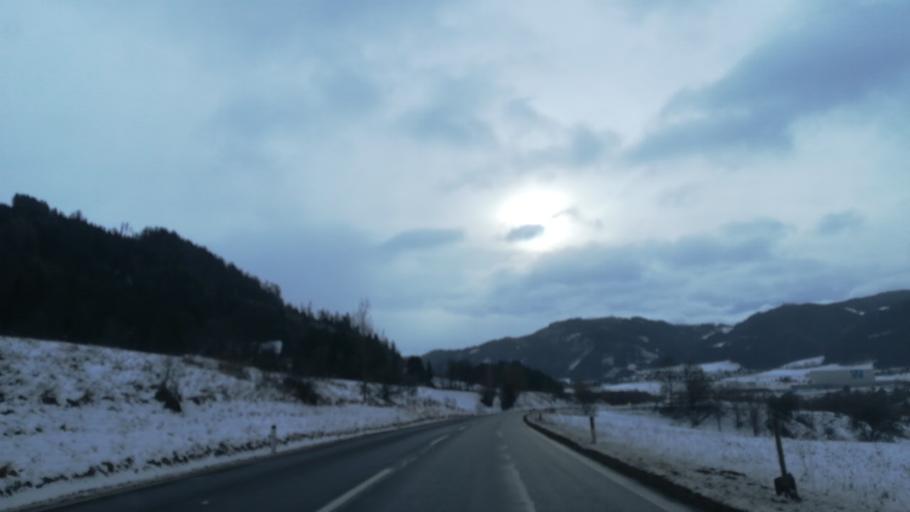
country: AT
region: Styria
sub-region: Politischer Bezirk Murtal
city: Sankt Peter ob Judenburg
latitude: 47.1958
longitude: 14.5966
